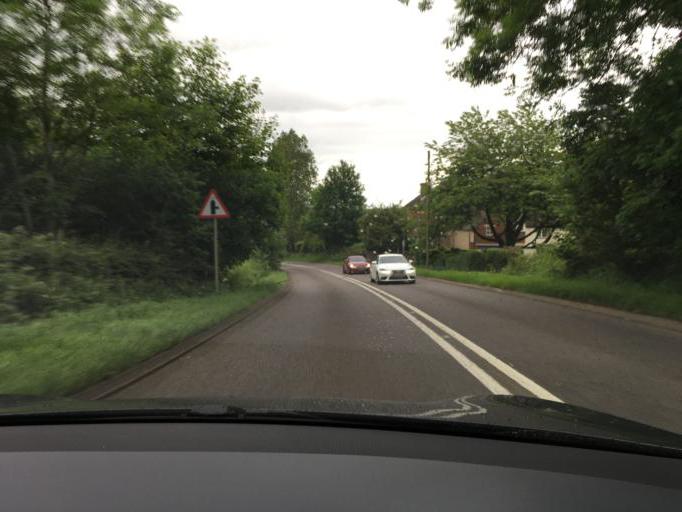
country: GB
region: England
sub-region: Staffordshire
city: Mayfield
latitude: 53.0129
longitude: -1.7725
